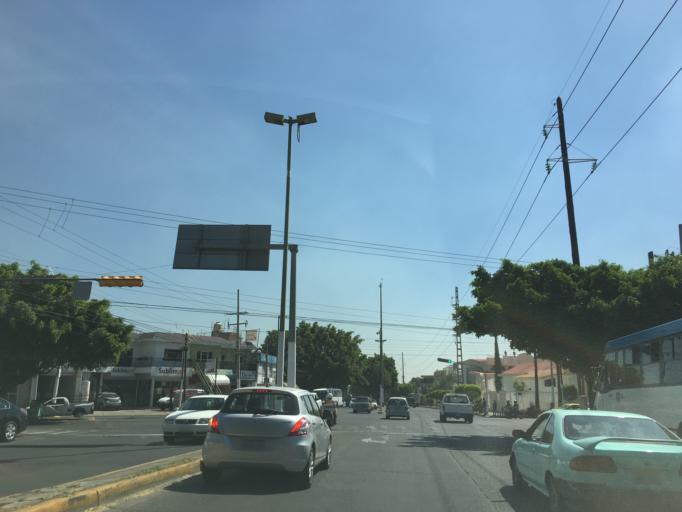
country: MX
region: Jalisco
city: Guadalajara
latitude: 20.6300
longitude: -103.4062
